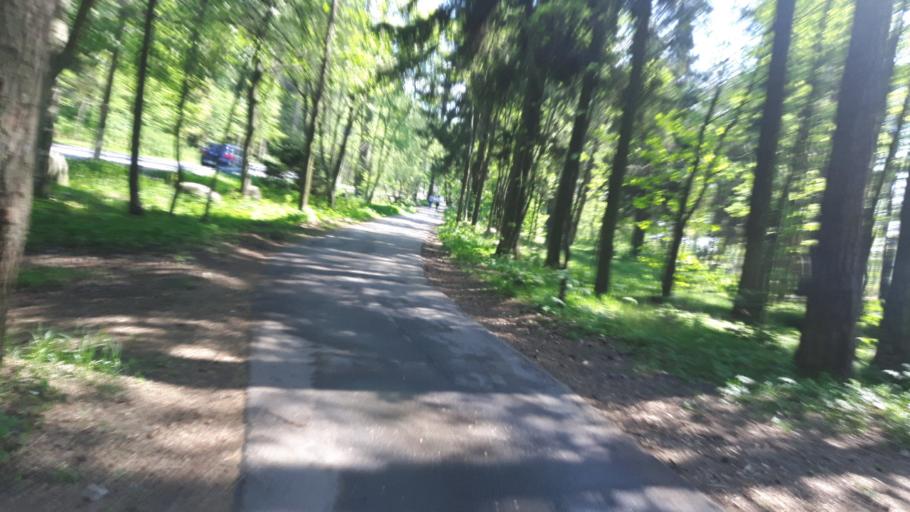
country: RU
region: St.-Petersburg
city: Komarovo
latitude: 60.1701
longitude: 29.8161
